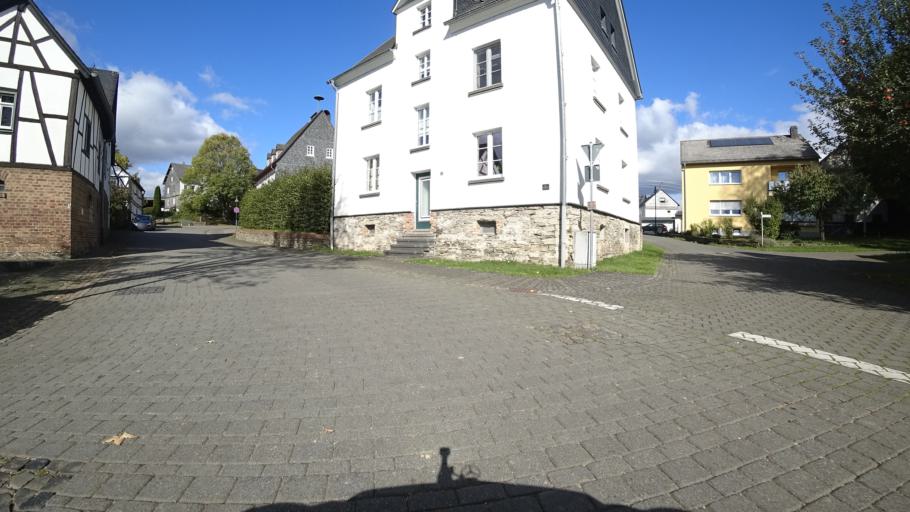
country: DE
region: Rheinland-Pfalz
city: Neuerkirch
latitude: 50.0141
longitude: 7.4914
